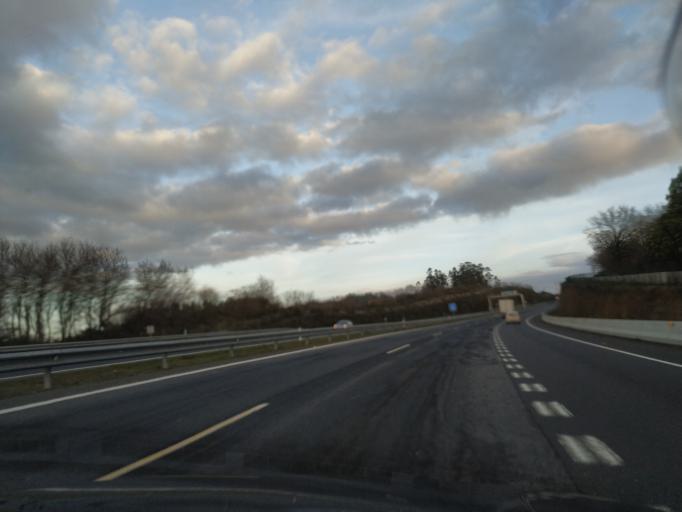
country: ES
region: Galicia
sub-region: Provincia da Coruna
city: Santiago de Compostela
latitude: 42.9007
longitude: -8.4929
